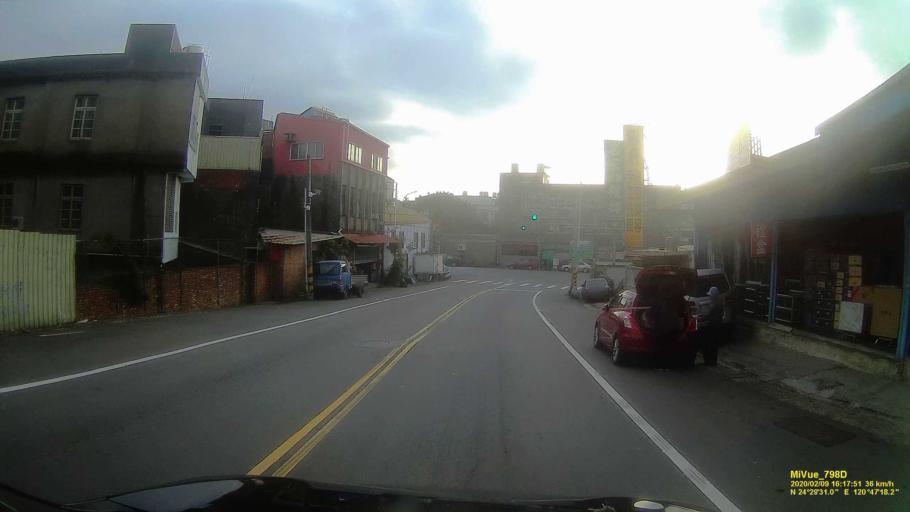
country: TW
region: Taiwan
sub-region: Miaoli
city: Miaoli
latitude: 24.4919
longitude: 120.7883
